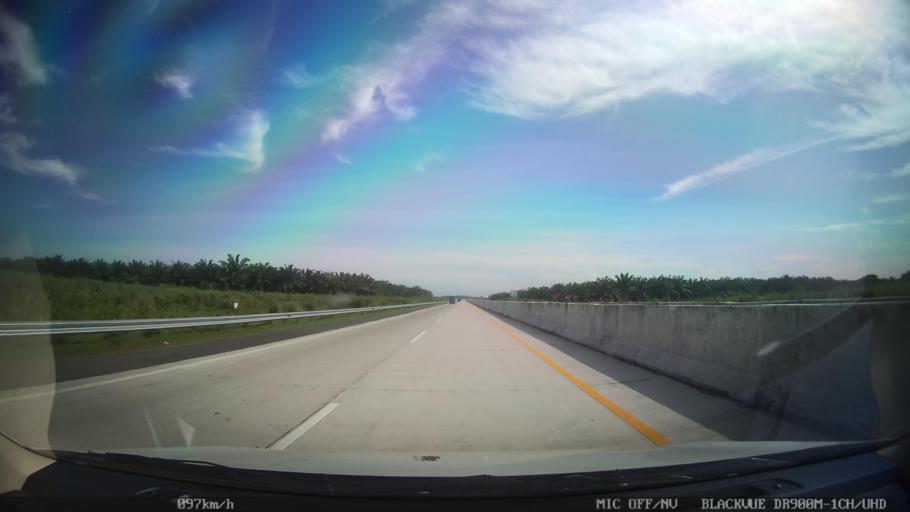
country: ID
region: North Sumatra
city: Binjai
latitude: 3.6853
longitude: 98.5384
